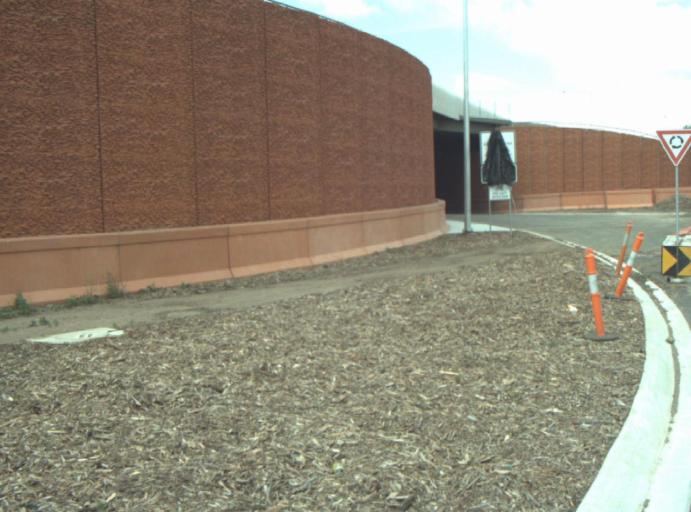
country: AU
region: Victoria
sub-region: Greater Geelong
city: Wandana Heights
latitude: -38.2036
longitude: 144.3028
